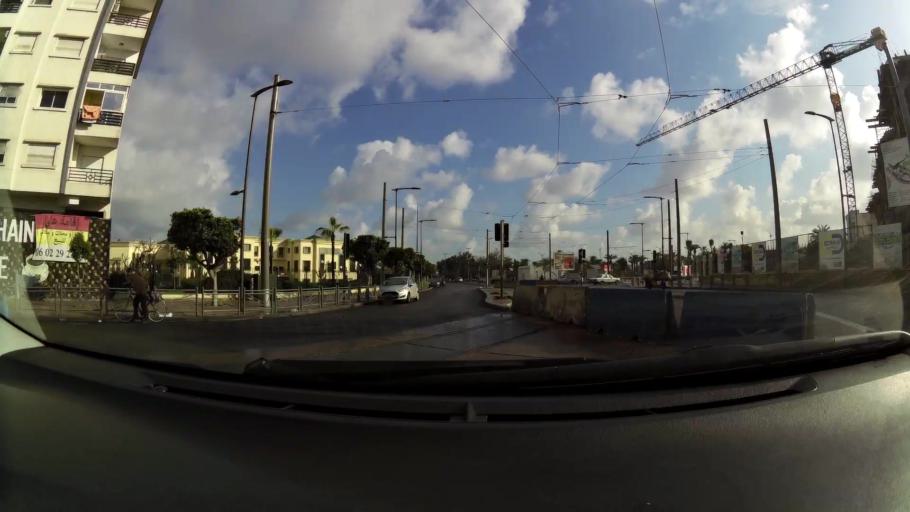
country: MA
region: Grand Casablanca
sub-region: Mediouna
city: Tit Mellil
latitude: 33.6001
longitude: -7.5310
